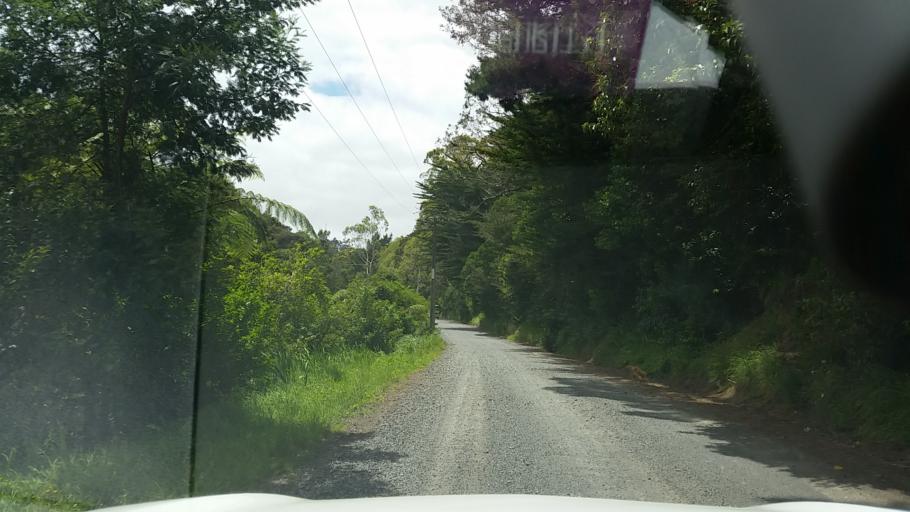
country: NZ
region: Auckland
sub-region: Auckland
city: Rosebank
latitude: -36.8522
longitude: 174.5908
